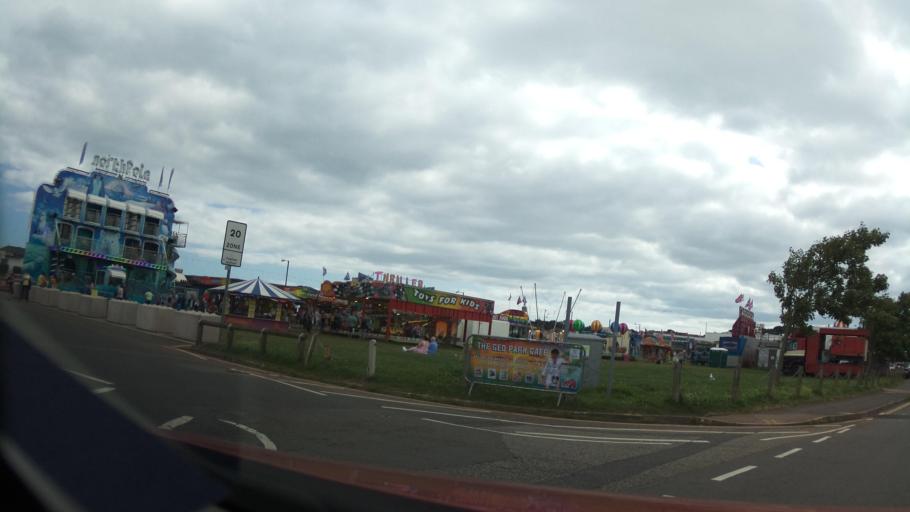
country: GB
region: England
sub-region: Borough of Torbay
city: Paignton
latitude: 50.4378
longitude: -3.5602
